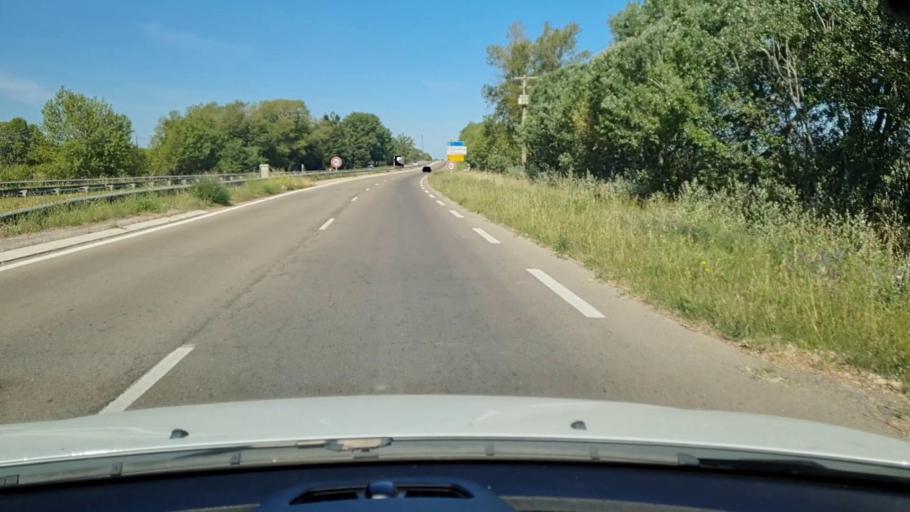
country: FR
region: Languedoc-Roussillon
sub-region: Departement du Gard
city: Le Grau-du-Roi
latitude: 43.5607
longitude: 4.1504
